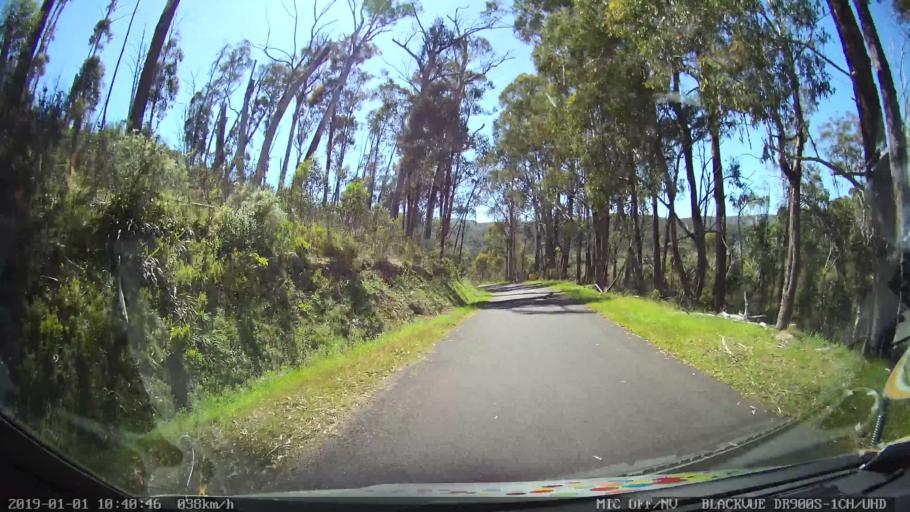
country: AU
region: New South Wales
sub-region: Snowy River
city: Jindabyne
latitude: -36.0368
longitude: 148.3149
